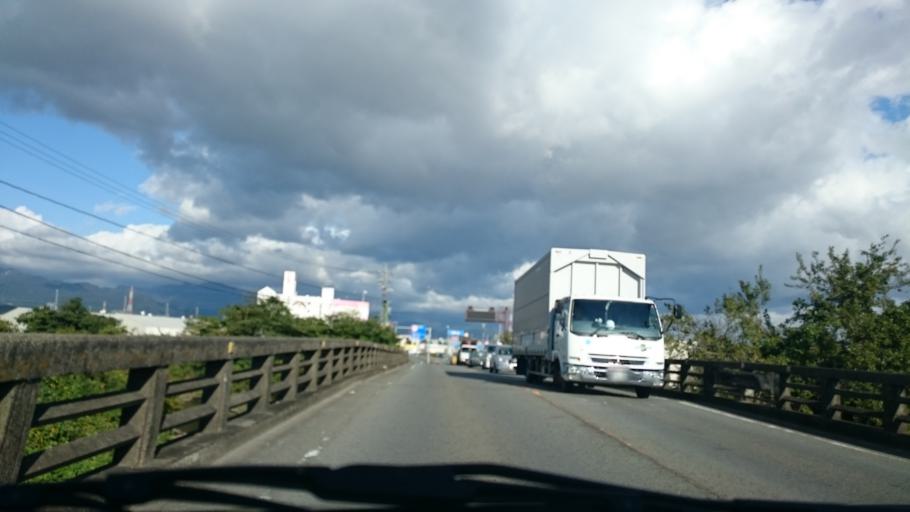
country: JP
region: Mie
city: Komono
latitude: 34.9851
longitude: 136.5547
